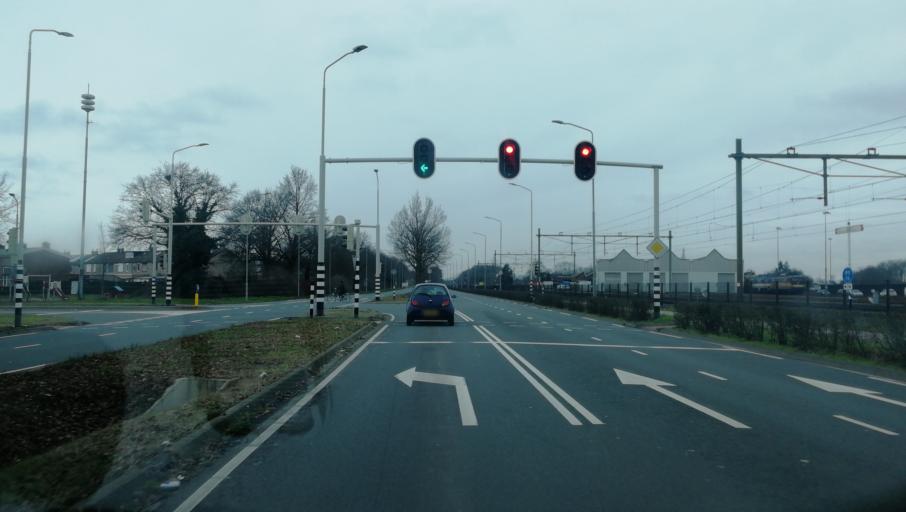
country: NL
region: Limburg
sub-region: Gemeente Venlo
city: Venlo
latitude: 51.3759
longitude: 6.1486
